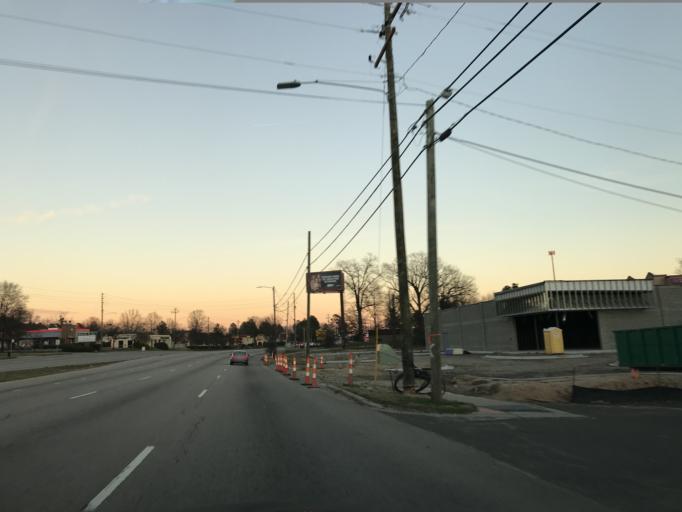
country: US
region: North Carolina
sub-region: Wake County
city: Raleigh
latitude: 35.7987
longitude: -78.5714
